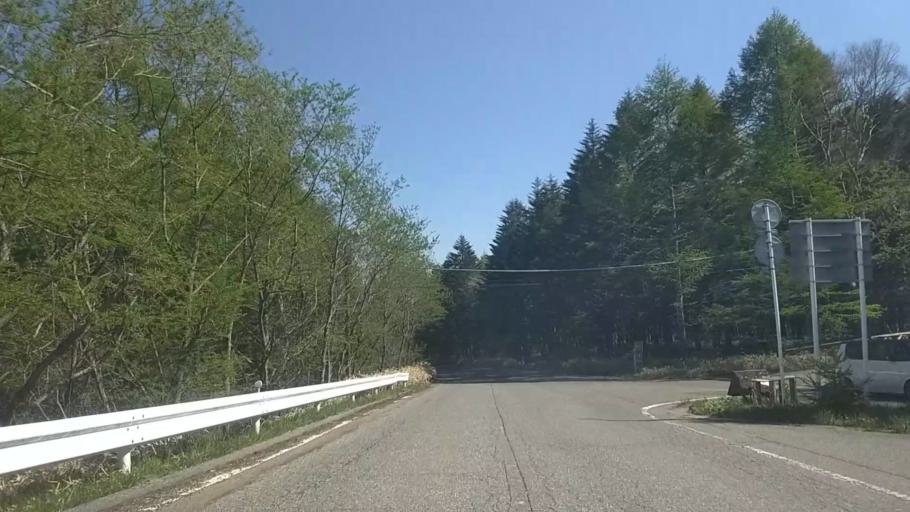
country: JP
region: Yamanashi
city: Nirasaki
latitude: 35.9451
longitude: 138.4195
